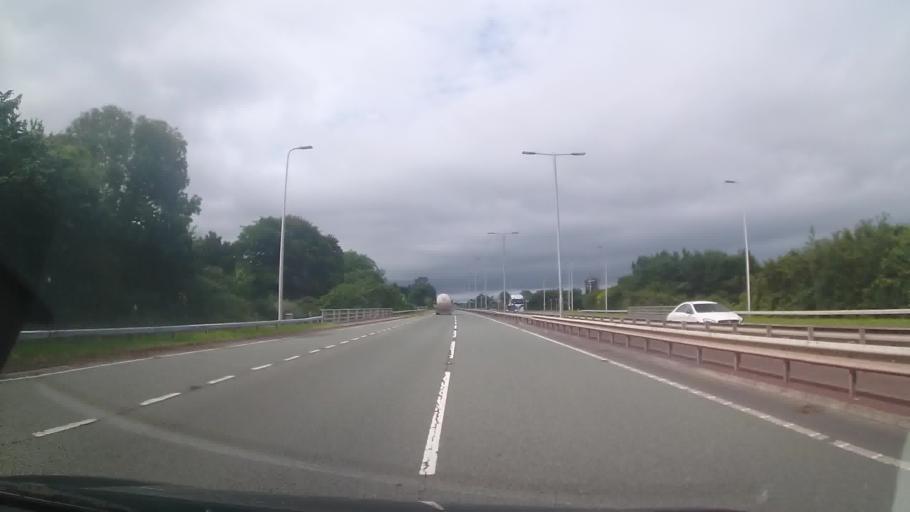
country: GB
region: Wales
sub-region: Gwynedd
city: Aber
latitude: 53.2349
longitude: -4.0173
